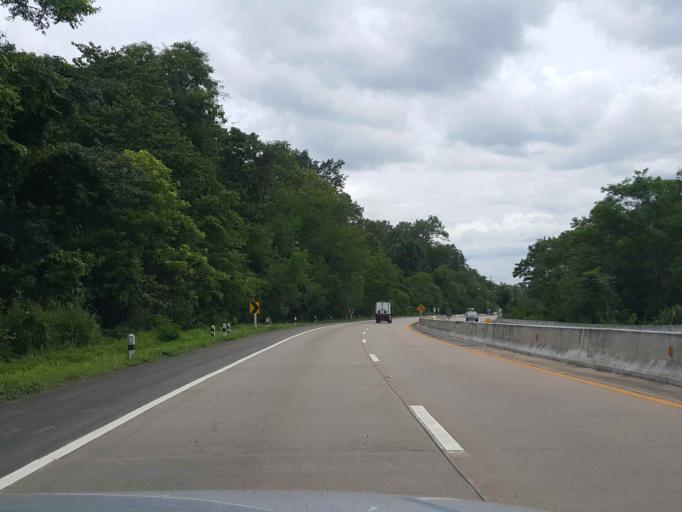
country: TH
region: Lampang
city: Hang Chat
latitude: 18.3727
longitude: 99.2353
